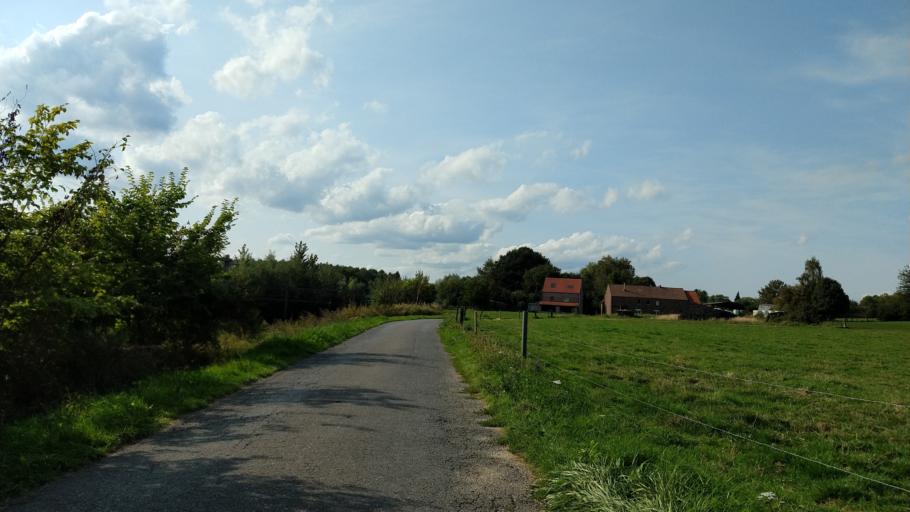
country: BE
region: Flanders
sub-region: Provincie Vlaams-Brabant
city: Boutersem
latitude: 50.8399
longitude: 4.8172
